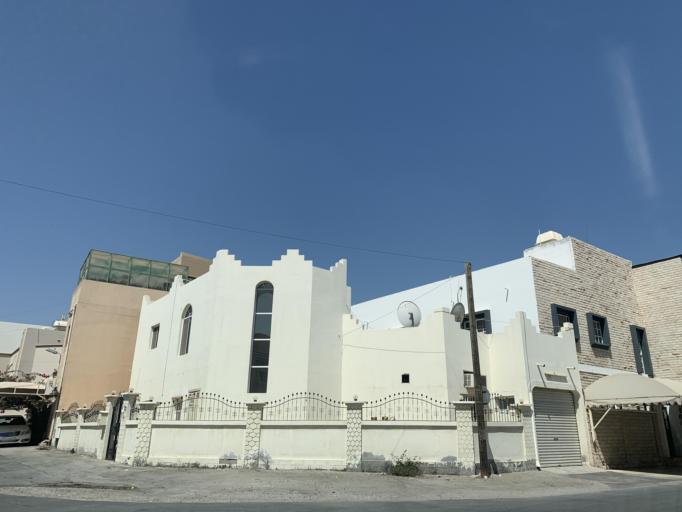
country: BH
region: Northern
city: Ar Rifa'
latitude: 26.1364
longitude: 50.5793
